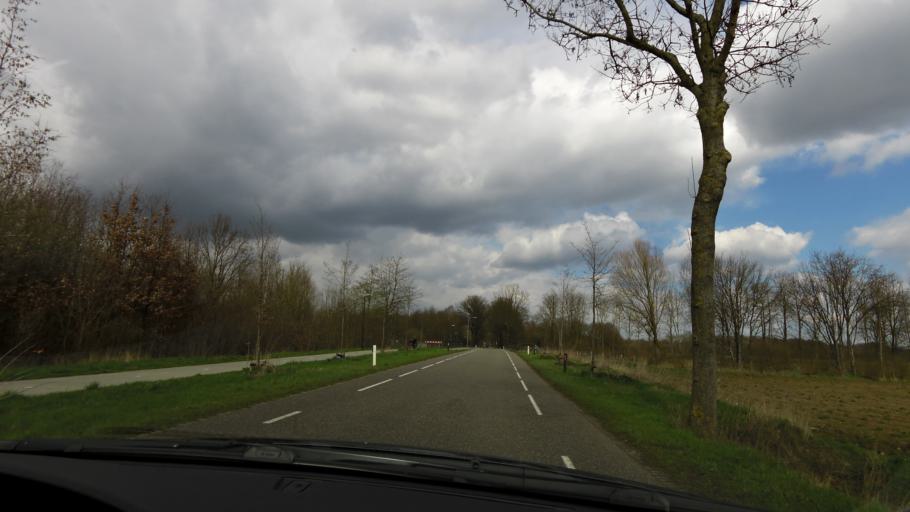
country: NL
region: Limburg
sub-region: Gemeente Sittard-Geleen
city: Limbricht
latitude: 51.0428
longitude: 5.8626
